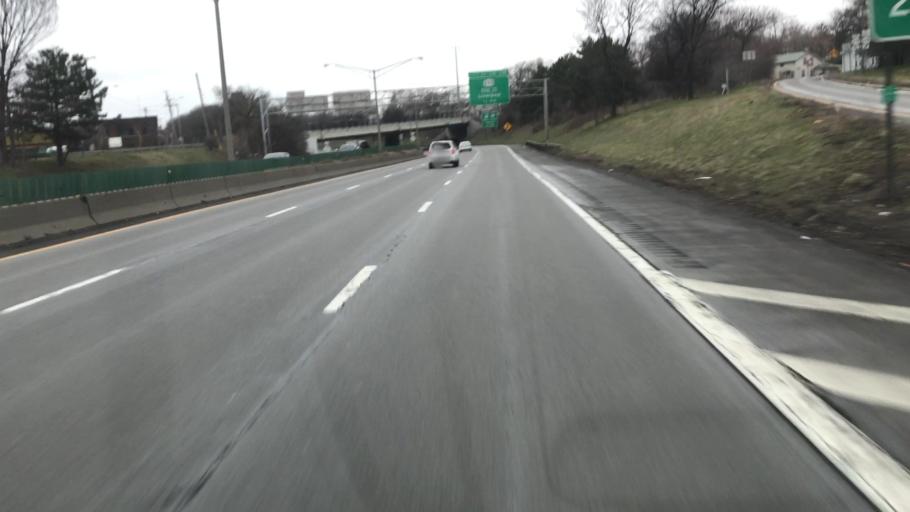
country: US
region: New York
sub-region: Onondaga County
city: Syracuse
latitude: 43.0633
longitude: -76.1587
